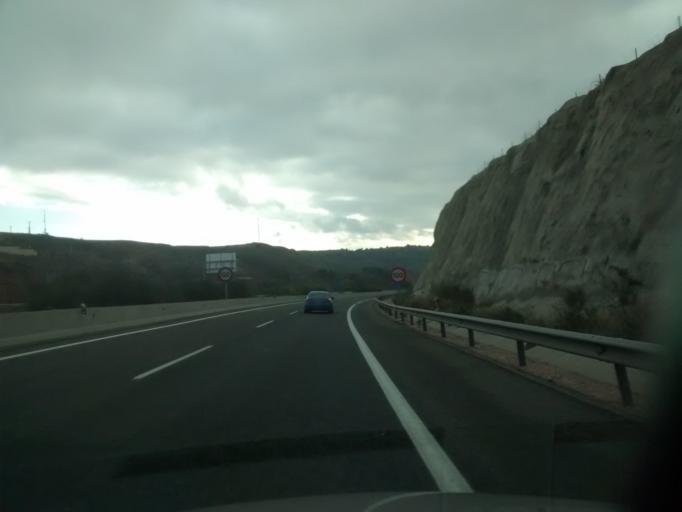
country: ES
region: Castille-La Mancha
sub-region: Provincia de Guadalajara
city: Torija
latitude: 40.7430
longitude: -3.0352
